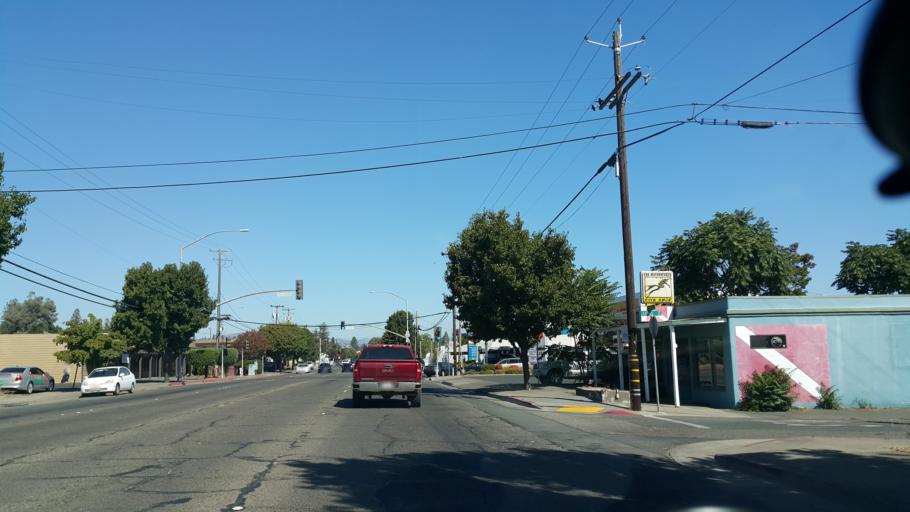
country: US
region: California
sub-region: Mendocino County
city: Ukiah
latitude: 39.1356
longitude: -123.2052
